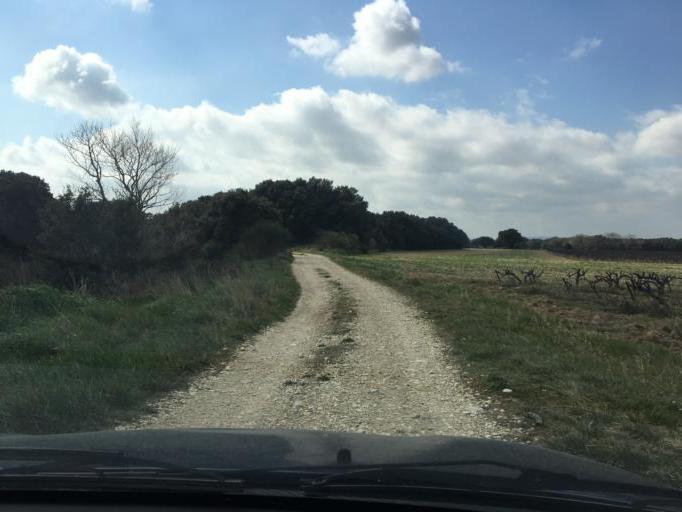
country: FR
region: Provence-Alpes-Cote d'Azur
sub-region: Departement du Vaucluse
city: Serignan-du-Comtat
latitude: 44.1671
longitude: 4.8241
